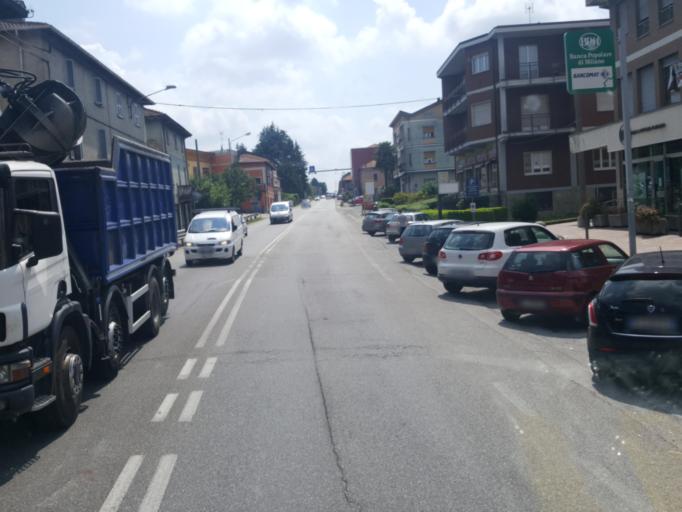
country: IT
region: Lombardy
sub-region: Provincia di Lecco
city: Calco
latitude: 45.7245
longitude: 9.4157
